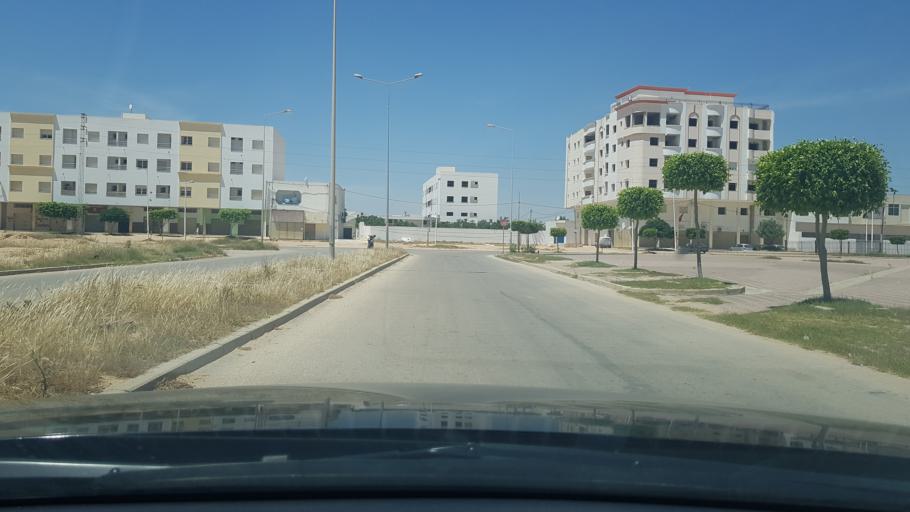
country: TN
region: Safaqis
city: Al Qarmadah
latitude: 34.8417
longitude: 10.7563
